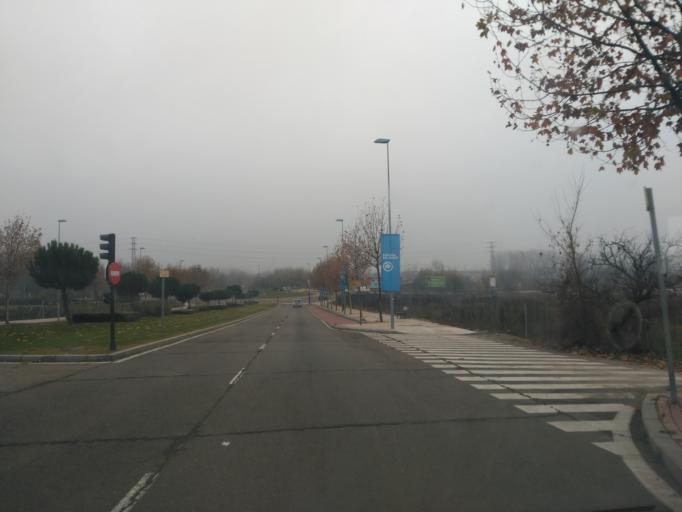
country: ES
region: Castille and Leon
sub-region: Provincia de Salamanca
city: Salamanca
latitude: 40.9629
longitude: -5.6458
